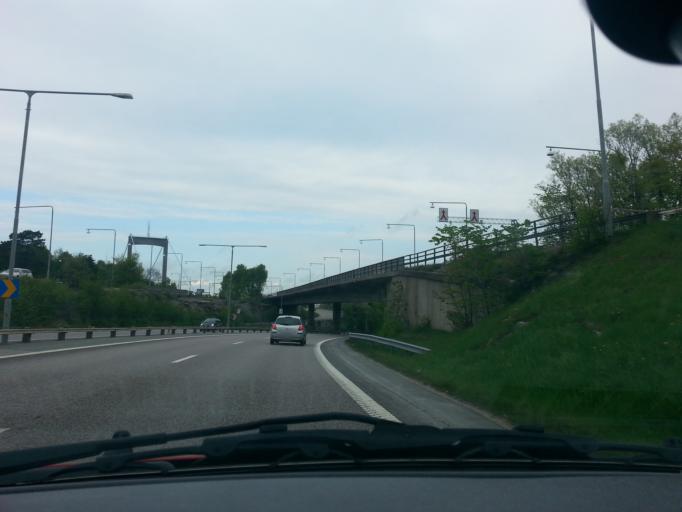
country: SE
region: Vaestra Goetaland
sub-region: Goteborg
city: Majorna
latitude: 57.6839
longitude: 11.9045
